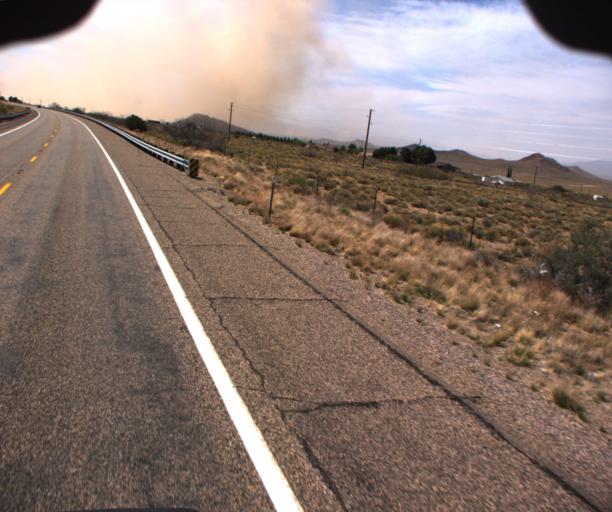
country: US
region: Arizona
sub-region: Mohave County
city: New Kingman-Butler
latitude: 35.4179
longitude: -113.7978
